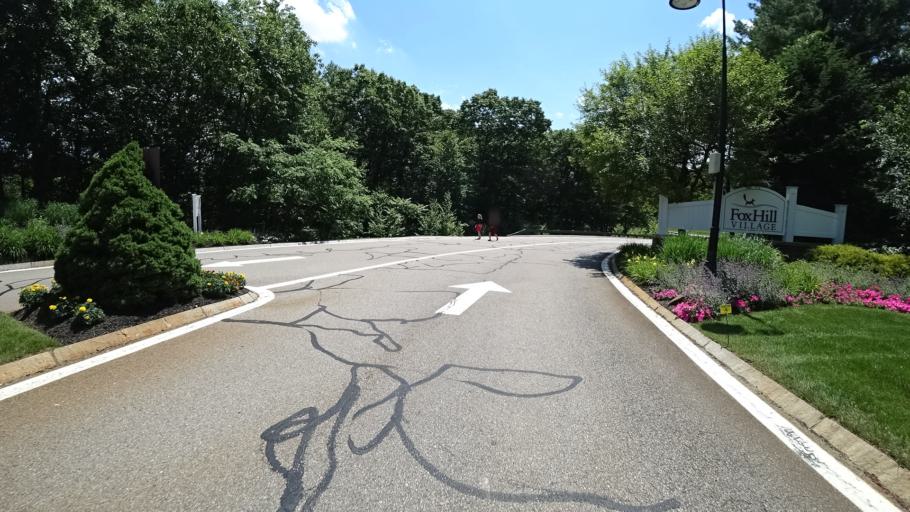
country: US
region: Massachusetts
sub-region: Norfolk County
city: Westwood
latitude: 42.2405
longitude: -71.2109
